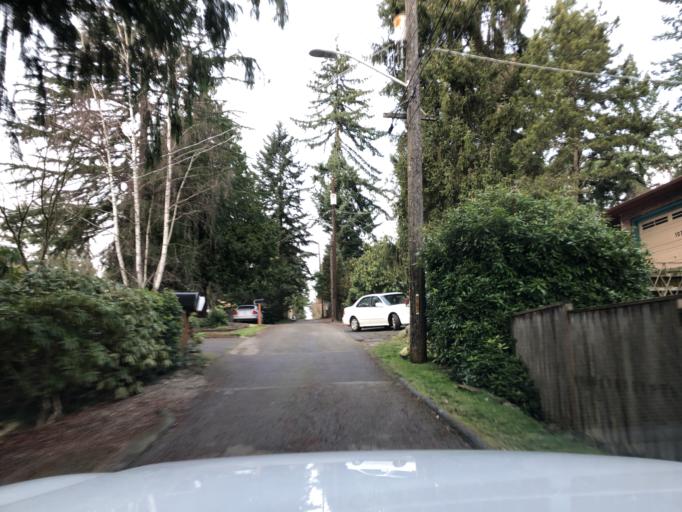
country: US
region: Washington
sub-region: King County
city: Lake Forest Park
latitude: 47.7076
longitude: -122.2810
